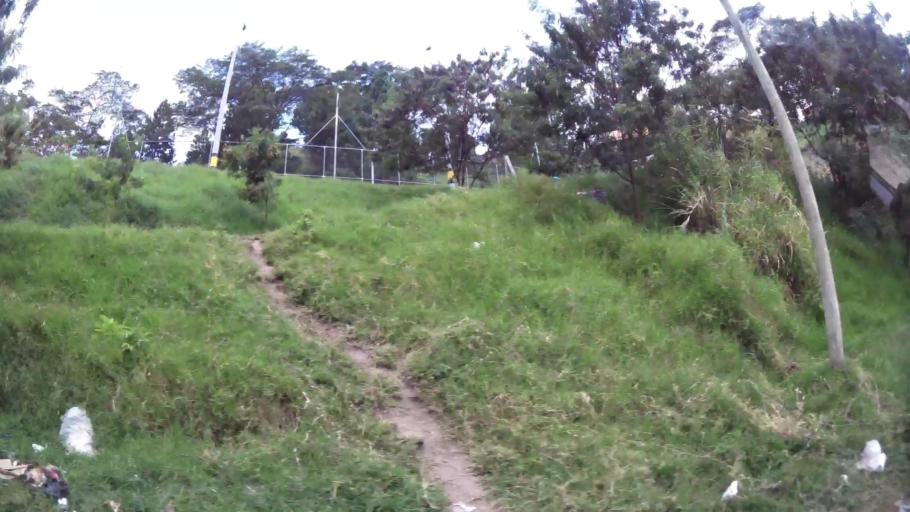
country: CO
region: Antioquia
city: Itagui
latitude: 6.1958
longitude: -75.6005
